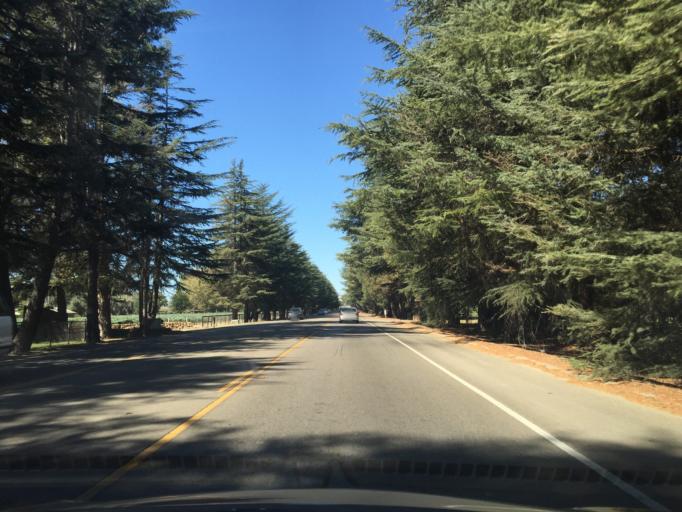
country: US
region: California
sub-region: Santa Barbara County
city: Buellton
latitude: 34.6025
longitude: -120.1671
